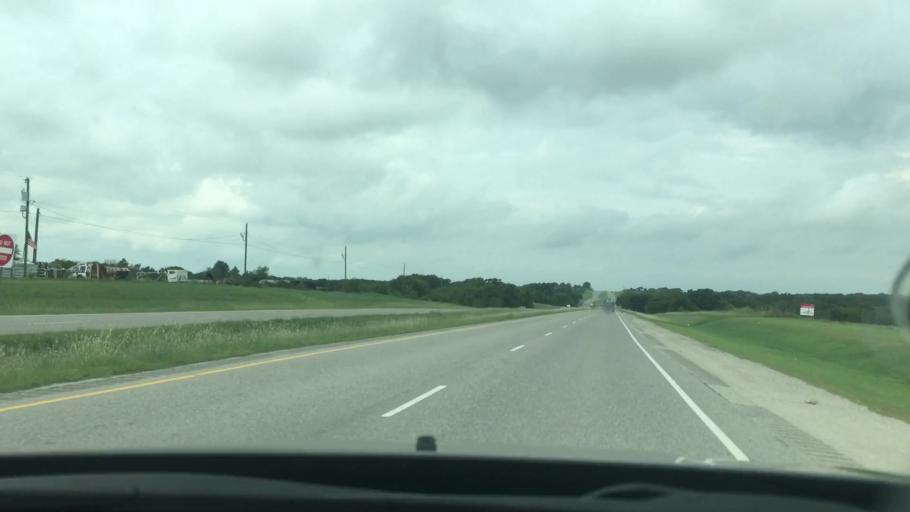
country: US
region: Oklahoma
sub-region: Carter County
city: Wilson
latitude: 34.1731
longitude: -97.4442
